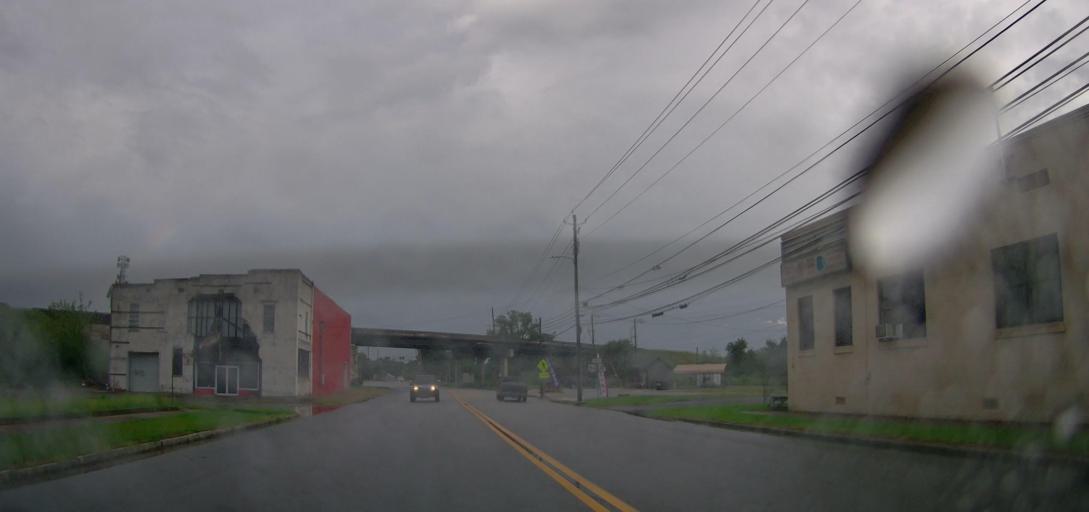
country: US
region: Georgia
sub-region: Ware County
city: Waycross
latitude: 31.2080
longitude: -82.3624
